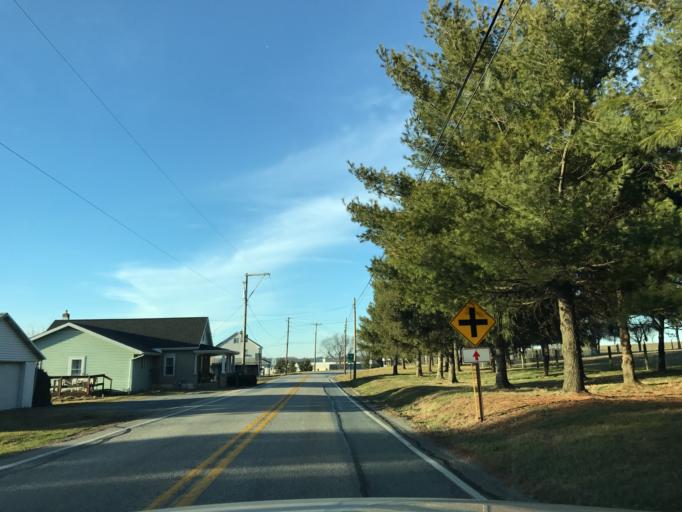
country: US
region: Pennsylvania
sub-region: Lancaster County
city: Maytown
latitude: 40.0898
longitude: -76.5921
